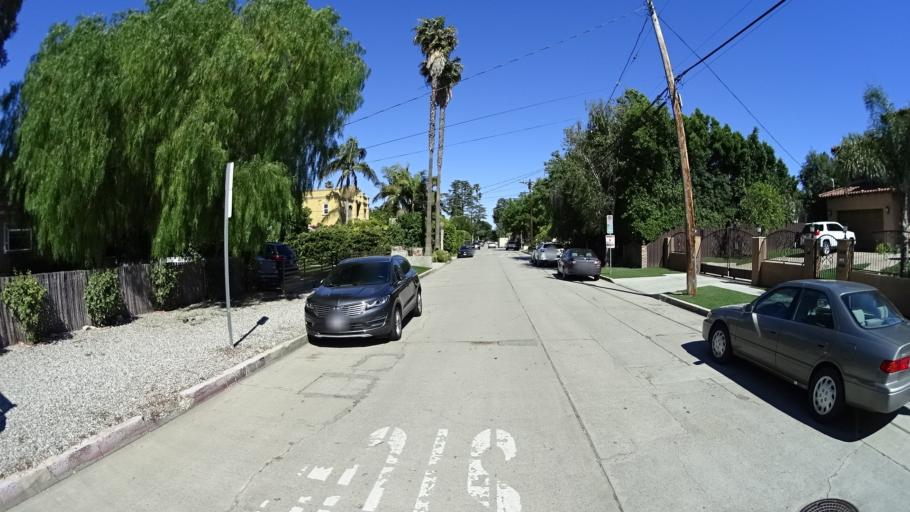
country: US
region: California
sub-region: Los Angeles County
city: Sherman Oaks
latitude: 34.1506
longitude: -118.4621
